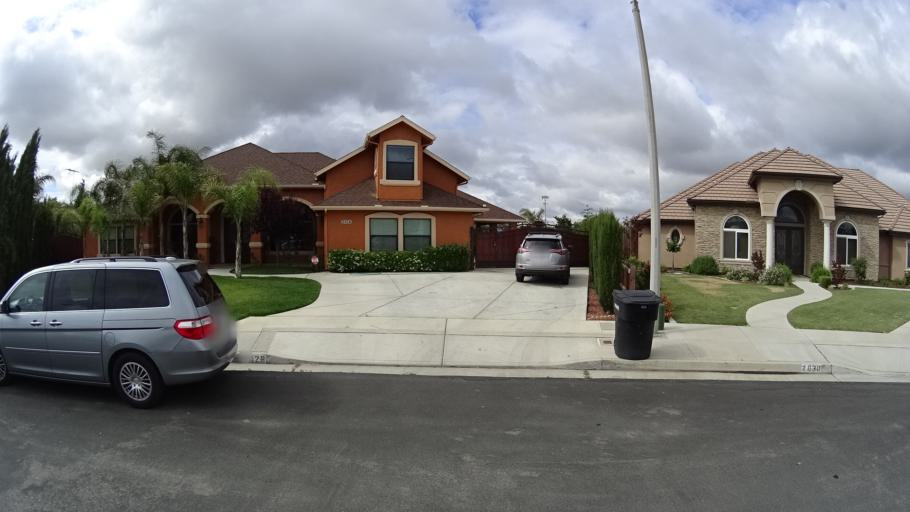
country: US
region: California
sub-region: Kings County
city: Hanford
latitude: 36.3483
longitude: -119.6667
